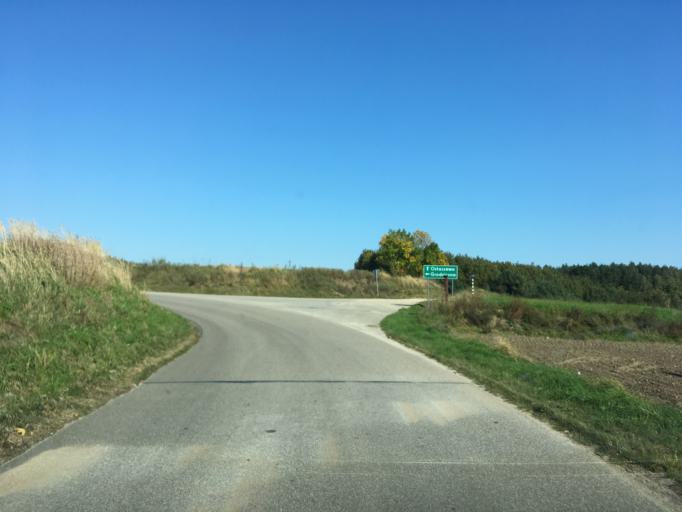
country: PL
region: Warmian-Masurian Voivodeship
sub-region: Powiat dzialdowski
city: Lidzbark
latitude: 53.3830
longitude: 19.7919
